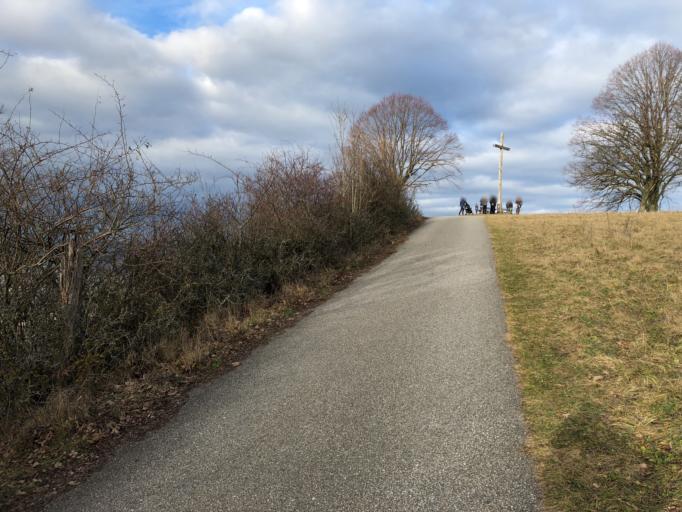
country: DE
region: Bavaria
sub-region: Upper Franconia
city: Kirchehrenbach
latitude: 49.7228
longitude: 11.1502
